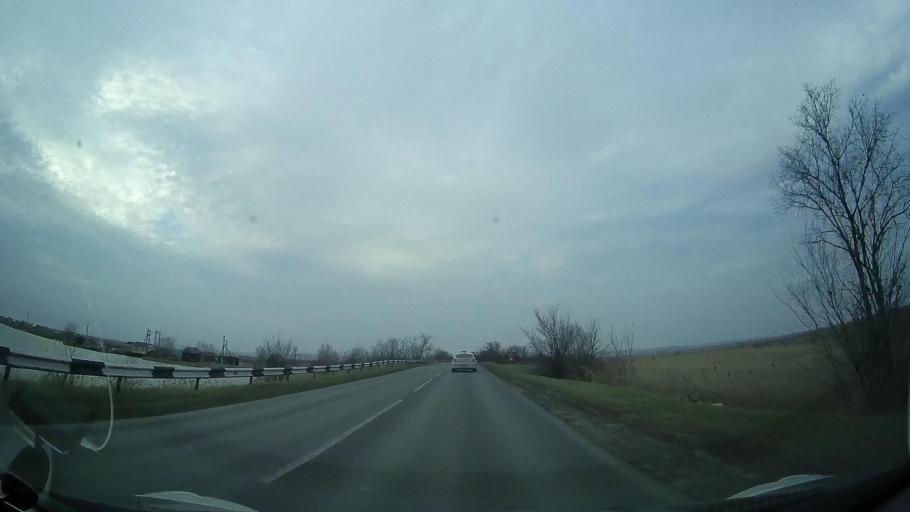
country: RU
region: Rostov
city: Ol'ginskaya
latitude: 47.2041
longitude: 39.9282
